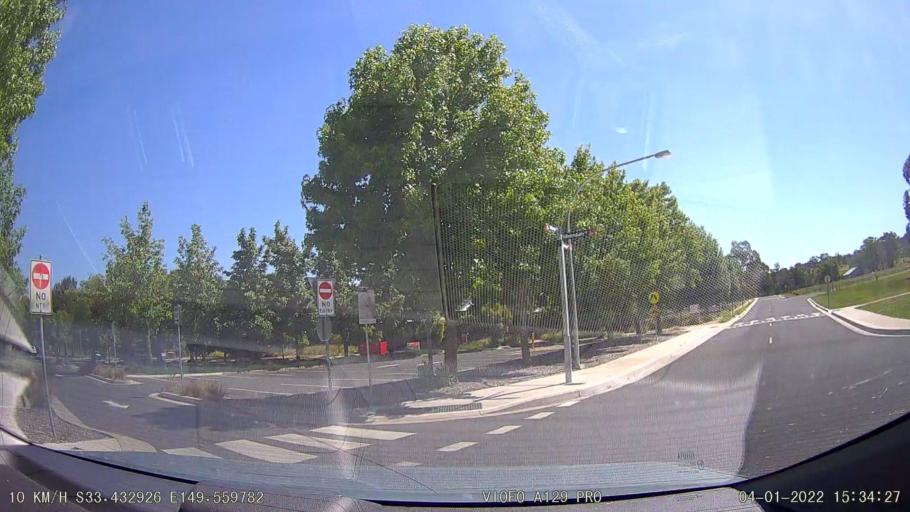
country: AU
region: New South Wales
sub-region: Bathurst Regional
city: Bathurst
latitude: -33.4330
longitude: 149.5597
